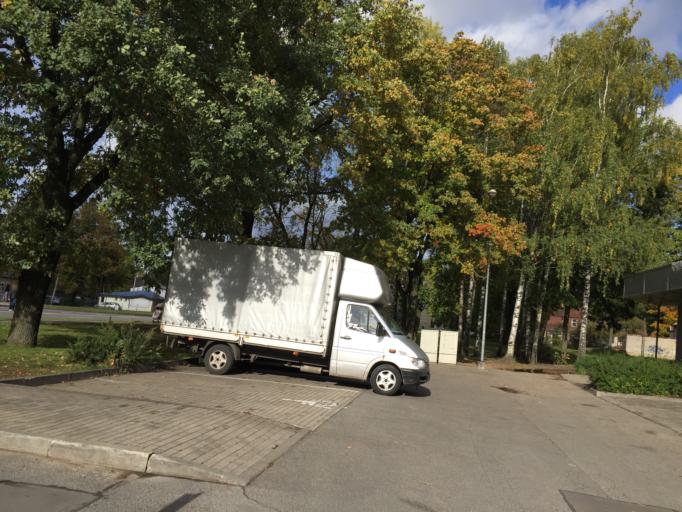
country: LV
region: Marupe
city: Marupe
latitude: 56.9593
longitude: 24.0527
